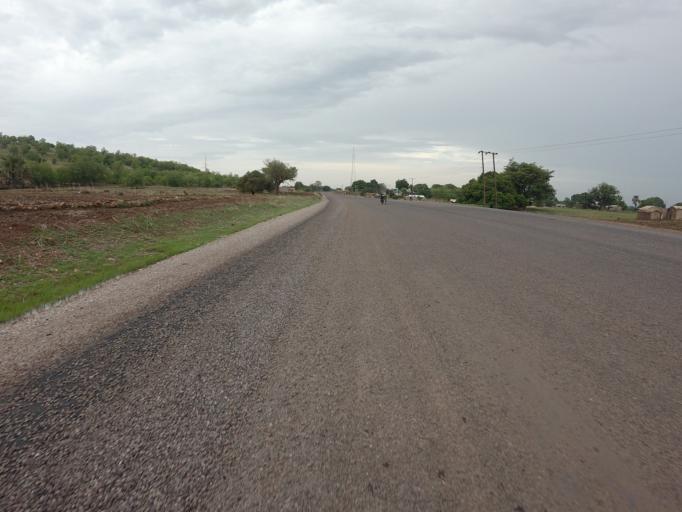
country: GH
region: Upper East
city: Bolgatanga
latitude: 10.8447
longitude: -0.6846
